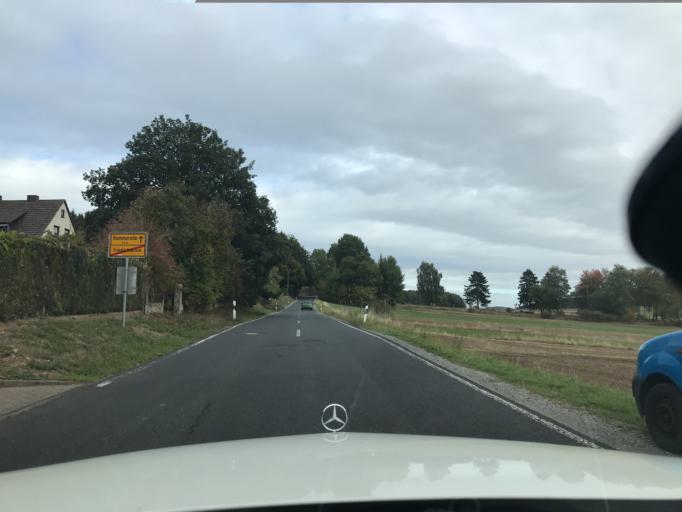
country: DE
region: Hesse
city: Hessisch Lichtenau
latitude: 51.2237
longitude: 9.7446
